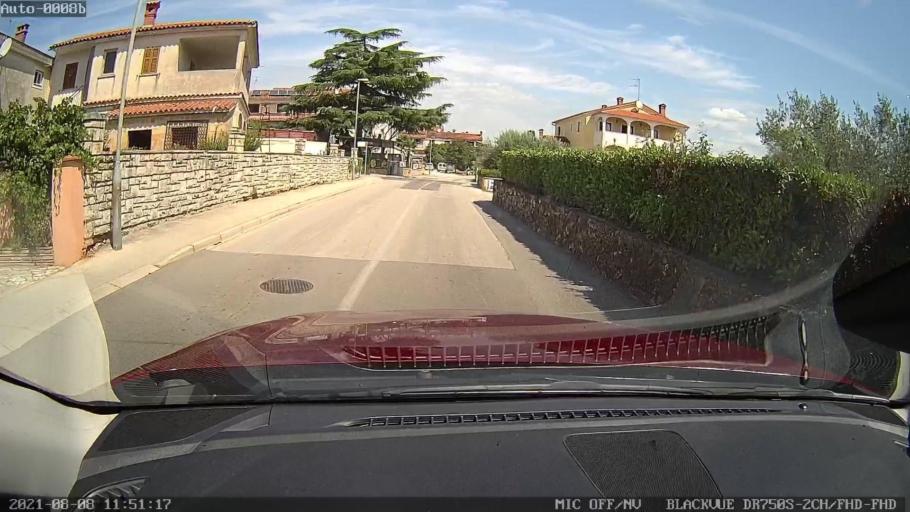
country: HR
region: Istarska
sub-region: Grad Rovinj
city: Rovinj
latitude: 45.0819
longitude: 13.6468
